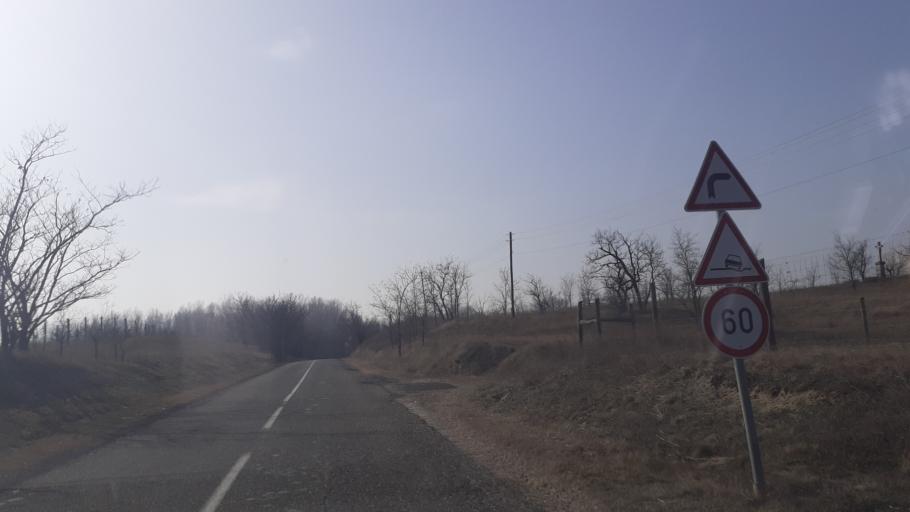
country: HU
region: Pest
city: Orkeny
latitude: 47.0494
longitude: 19.3252
